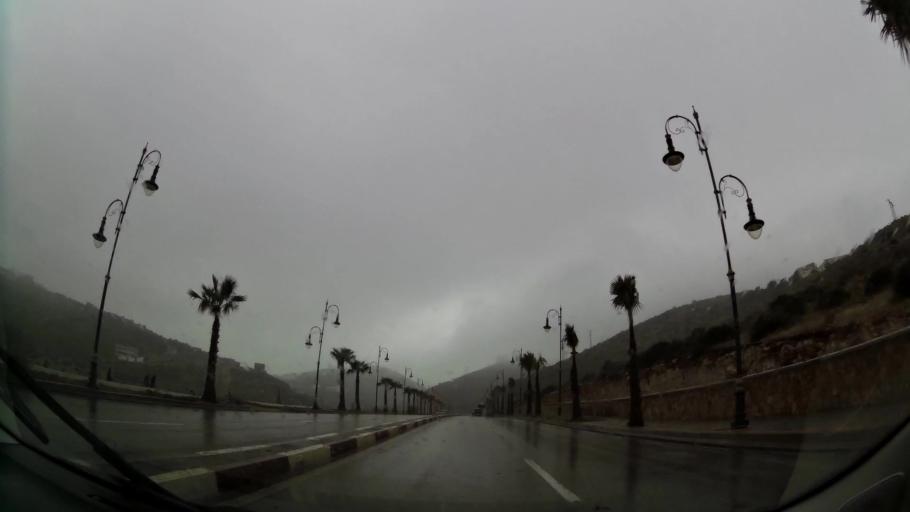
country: MA
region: Taza-Al Hoceima-Taounate
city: Tirhanimine
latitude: 35.2135
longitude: -3.9188
